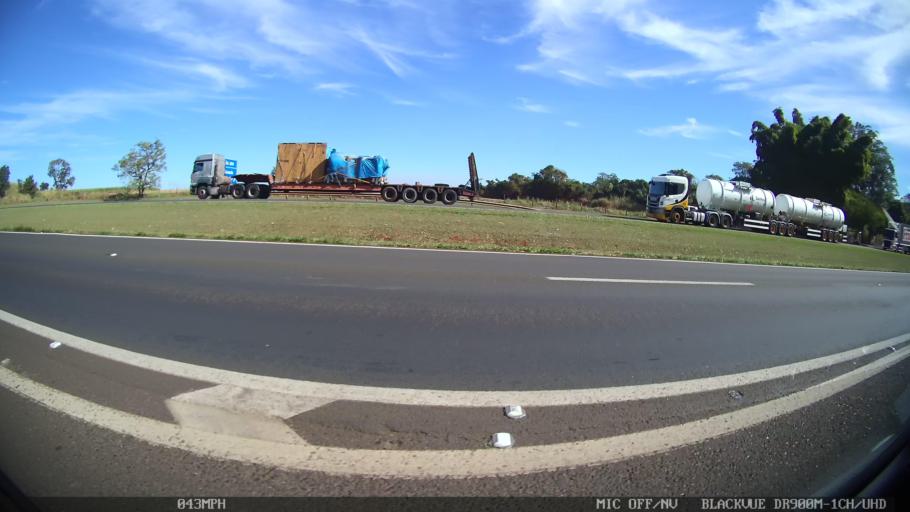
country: BR
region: Sao Paulo
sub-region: Araraquara
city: Araraquara
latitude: -21.8337
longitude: -48.1569
